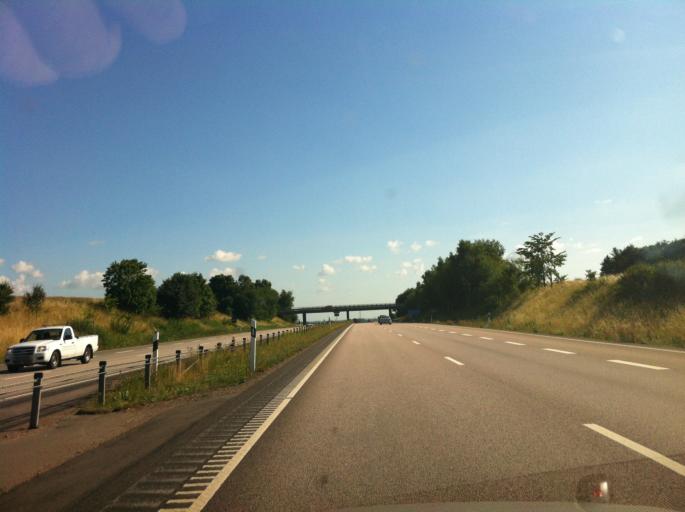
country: SE
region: Skane
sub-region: Helsingborg
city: Hyllinge
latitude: 56.1021
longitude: 12.7995
